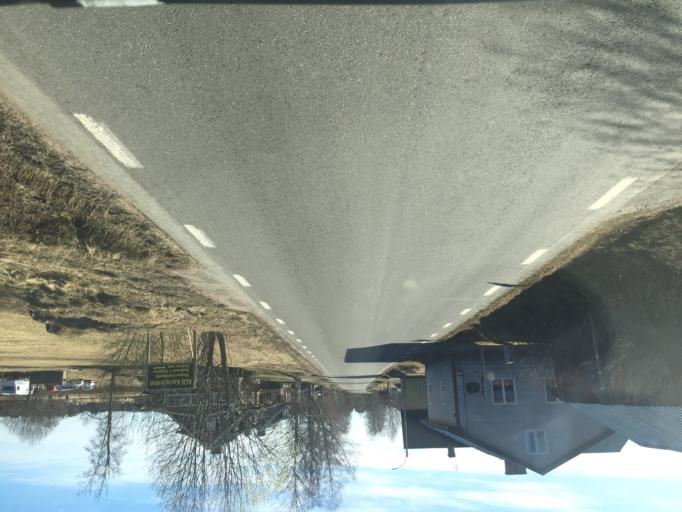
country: SE
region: Dalarna
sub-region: Vansbro Kommun
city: Vansbro
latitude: 60.4593
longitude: 13.9959
